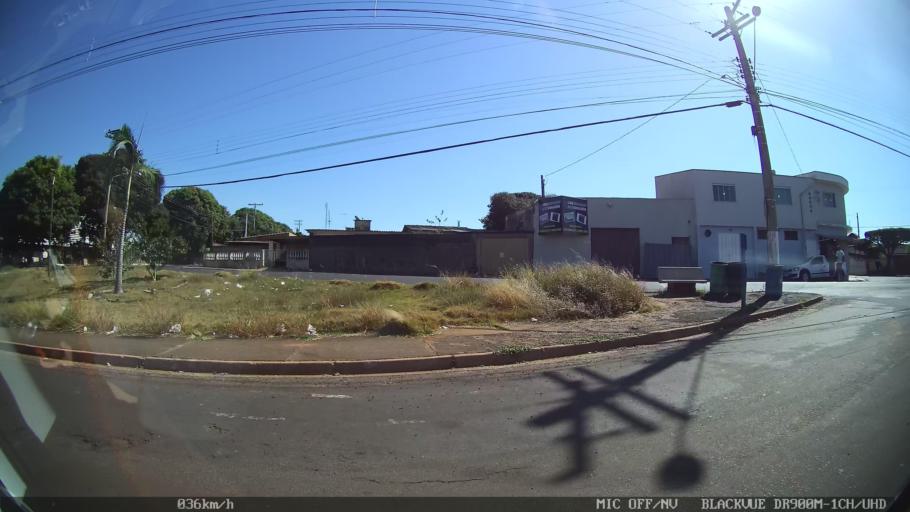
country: BR
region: Sao Paulo
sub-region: Batatais
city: Batatais
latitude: -20.8862
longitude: -47.5726
